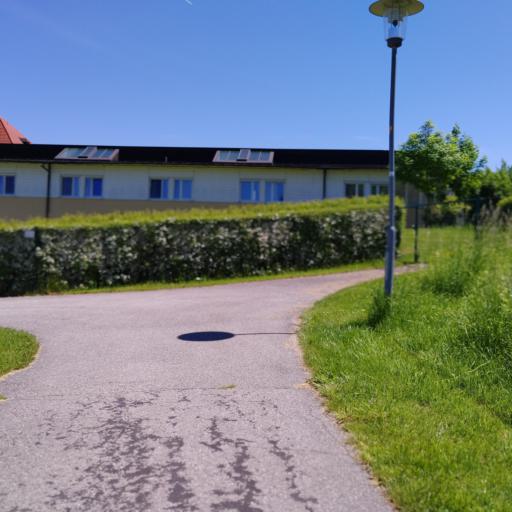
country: AT
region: Lower Austria
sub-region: Politischer Bezirk Sankt Polten
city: Maria-Anzbach
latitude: 48.1873
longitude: 15.9408
